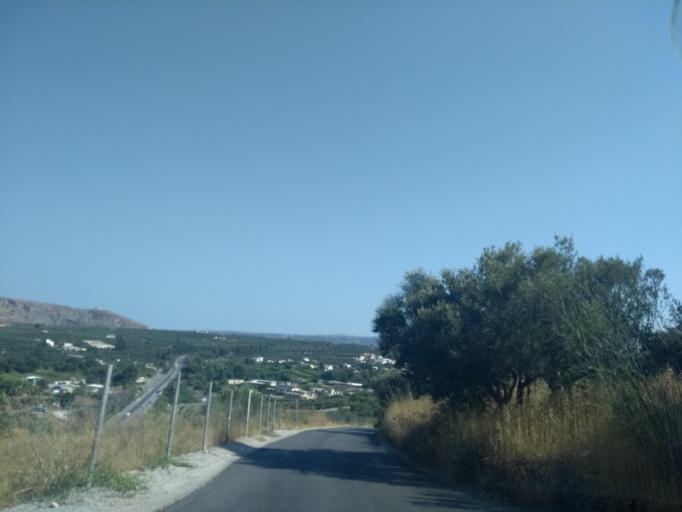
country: GR
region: Crete
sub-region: Nomos Chanias
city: Kalivai
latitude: 35.4406
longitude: 24.1722
